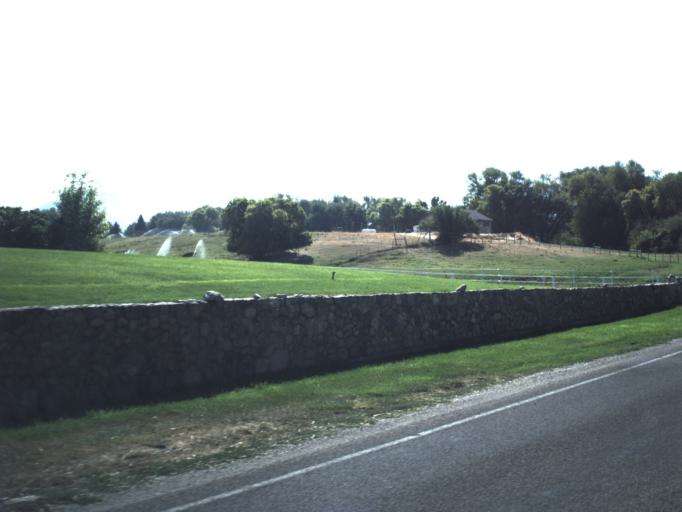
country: US
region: Utah
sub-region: Cache County
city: Hyrum
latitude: 41.5762
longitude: -111.8384
